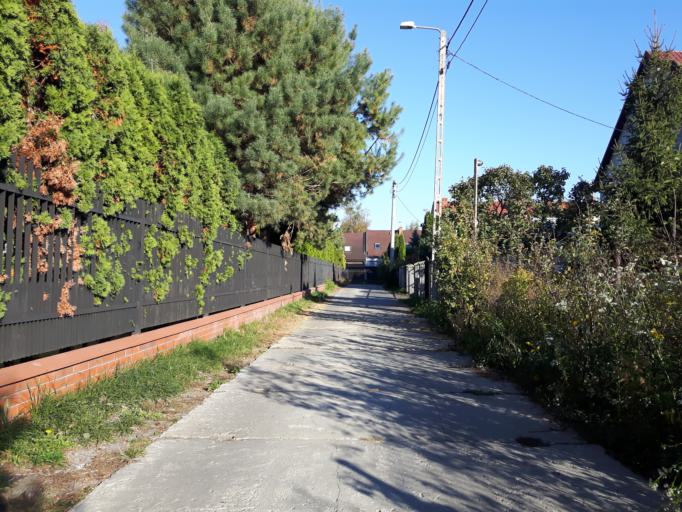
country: PL
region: Masovian Voivodeship
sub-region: Powiat wolominski
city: Zabki
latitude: 52.2861
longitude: 21.1314
